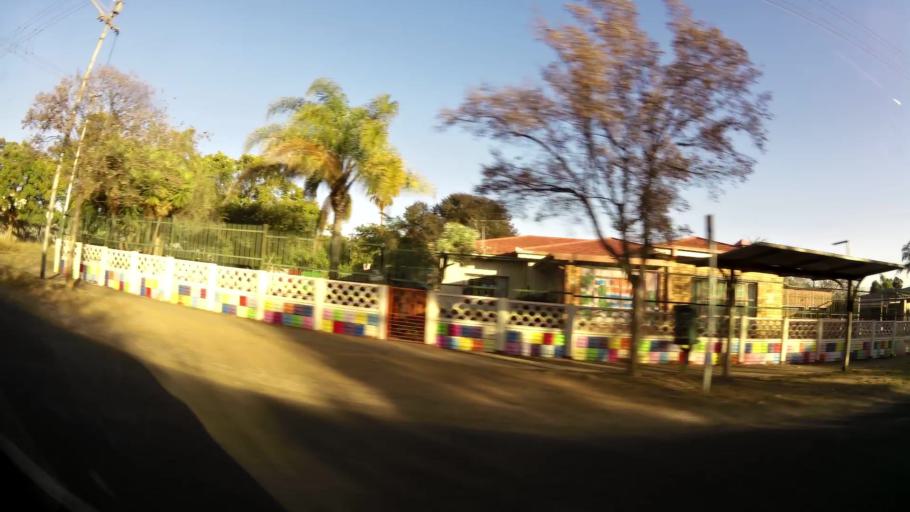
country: ZA
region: Gauteng
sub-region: City of Tshwane Metropolitan Municipality
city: Pretoria
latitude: -25.7051
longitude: 28.2226
